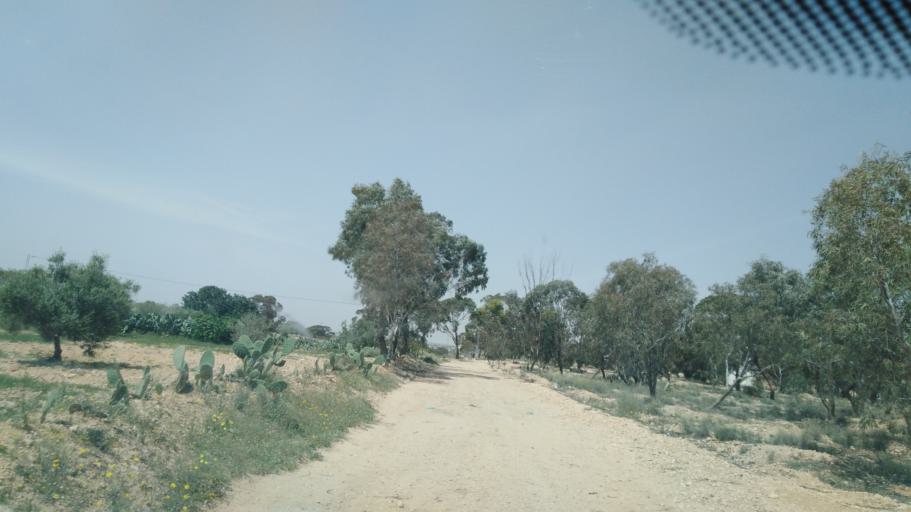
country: TN
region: Safaqis
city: Sfax
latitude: 34.7220
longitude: 10.5730
